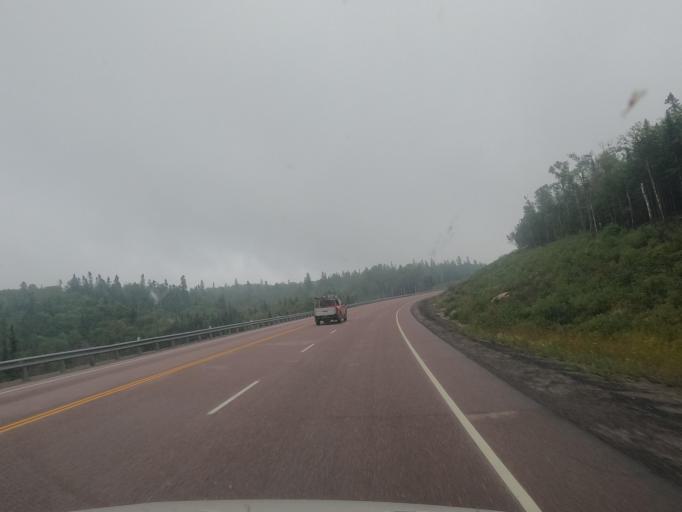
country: CA
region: Ontario
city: Greenstone
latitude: 48.9079
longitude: -87.6556
